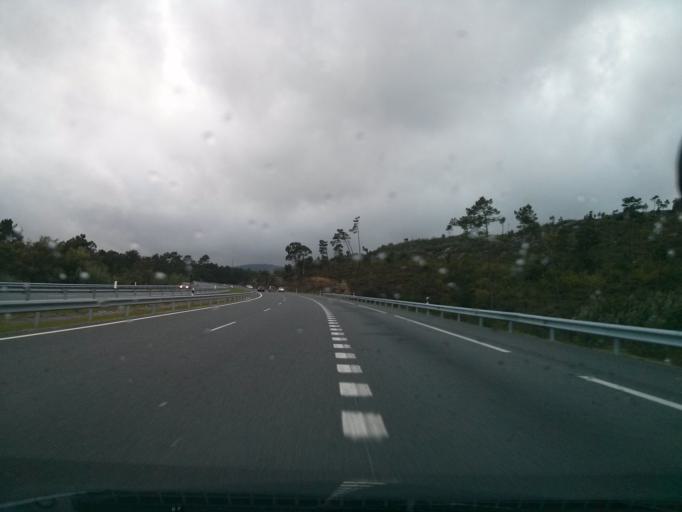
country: ES
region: Galicia
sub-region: Provincia de Ourense
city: Carballeda de Avia
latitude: 42.2973
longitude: -8.1860
